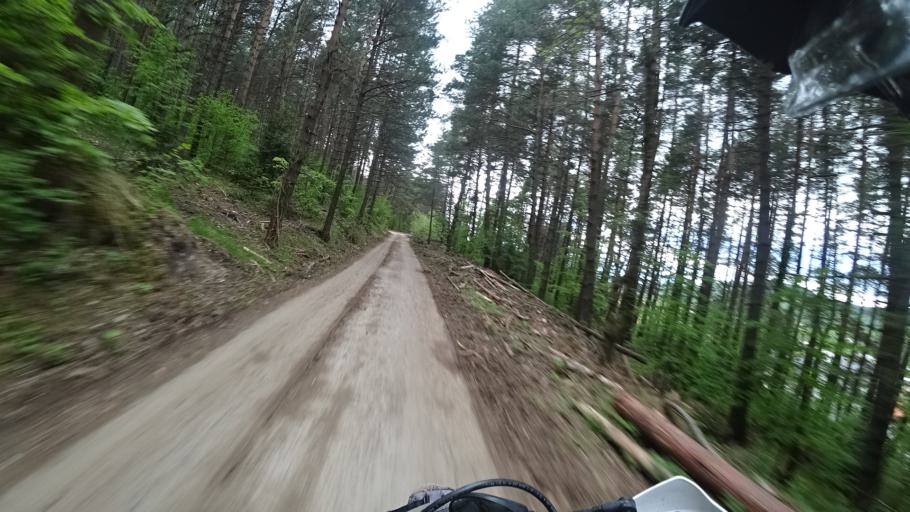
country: HR
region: Licko-Senjska
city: Otocac
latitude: 44.8483
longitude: 15.4271
